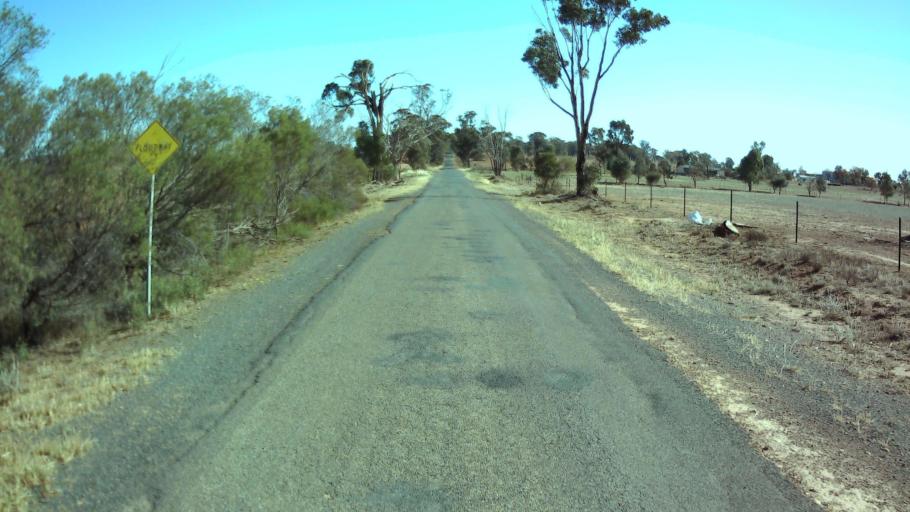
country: AU
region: New South Wales
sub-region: Weddin
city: Grenfell
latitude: -33.7943
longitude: 147.9569
